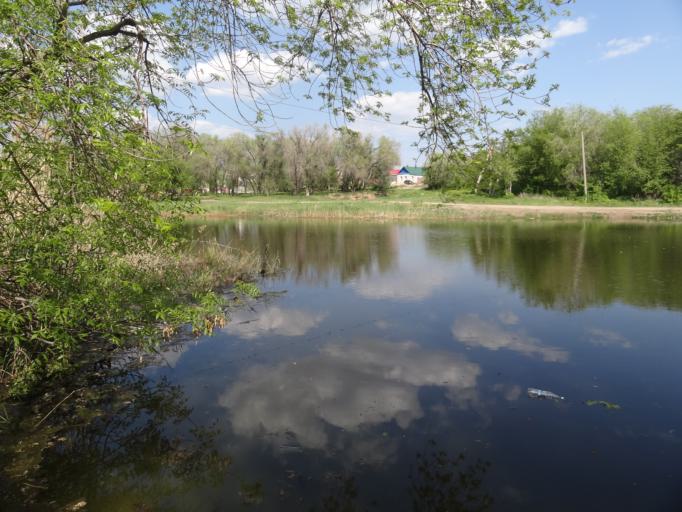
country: RU
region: Saratov
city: Engel's
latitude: 51.4993
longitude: 46.1020
